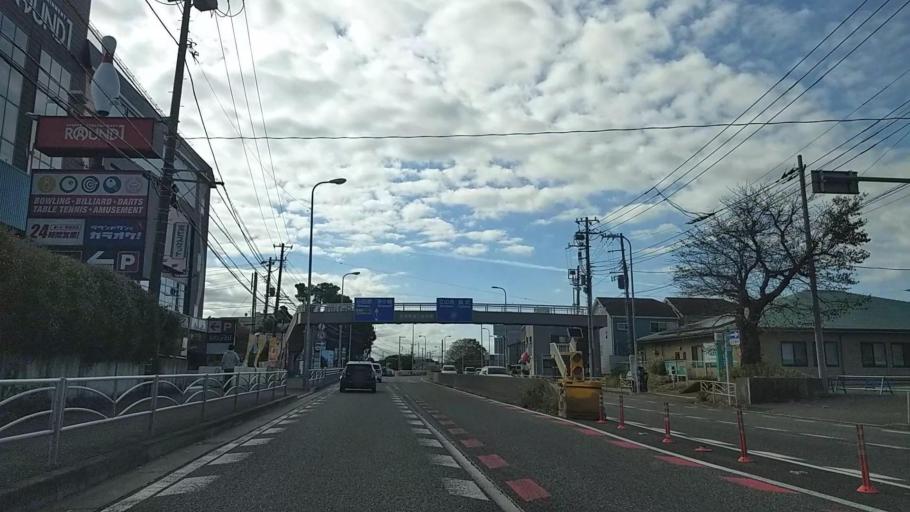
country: JP
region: Kanagawa
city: Fujisawa
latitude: 35.3644
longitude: 139.4975
